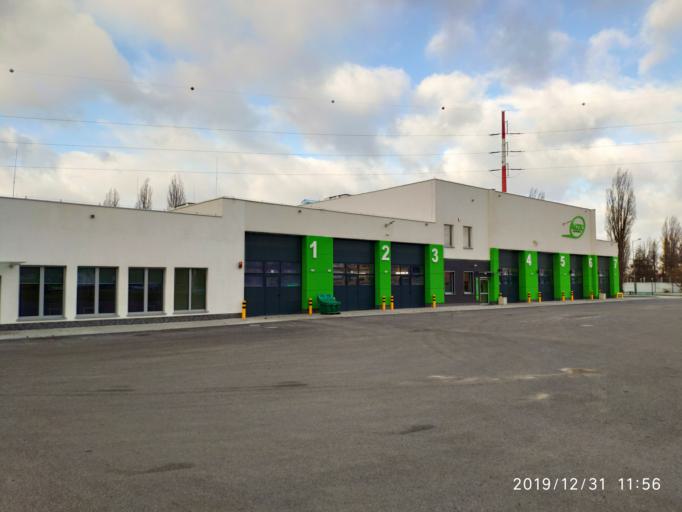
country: PL
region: Lubusz
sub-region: Zielona Gora
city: Zielona Gora
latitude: 51.9510
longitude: 15.4831
